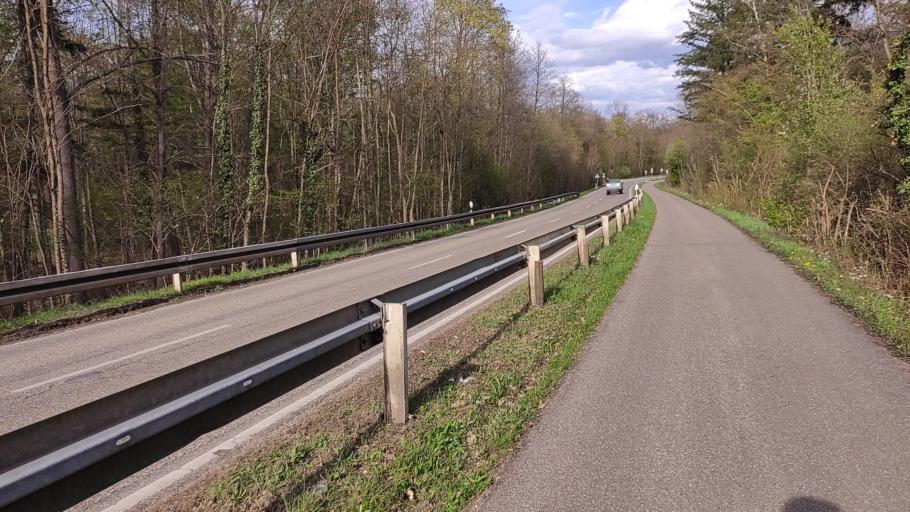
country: DE
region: Baden-Wuerttemberg
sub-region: Freiburg Region
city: Umkirch
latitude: 47.9987
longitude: 7.7585
